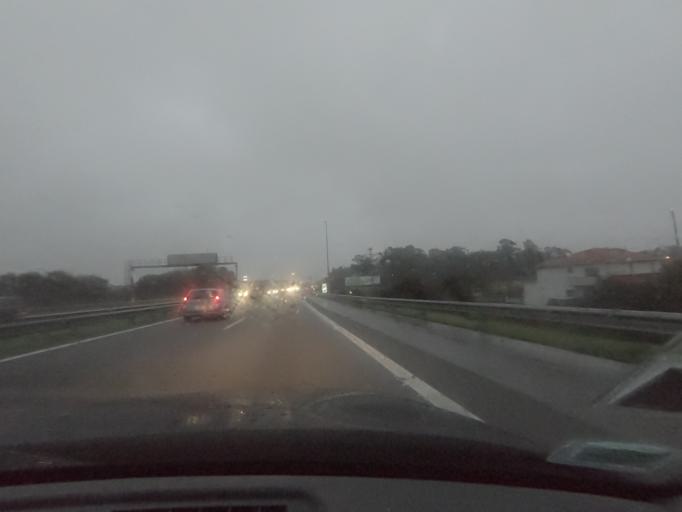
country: PT
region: Porto
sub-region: Matosinhos
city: Santa Cruz do Bispo
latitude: 41.2237
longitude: -8.6934
